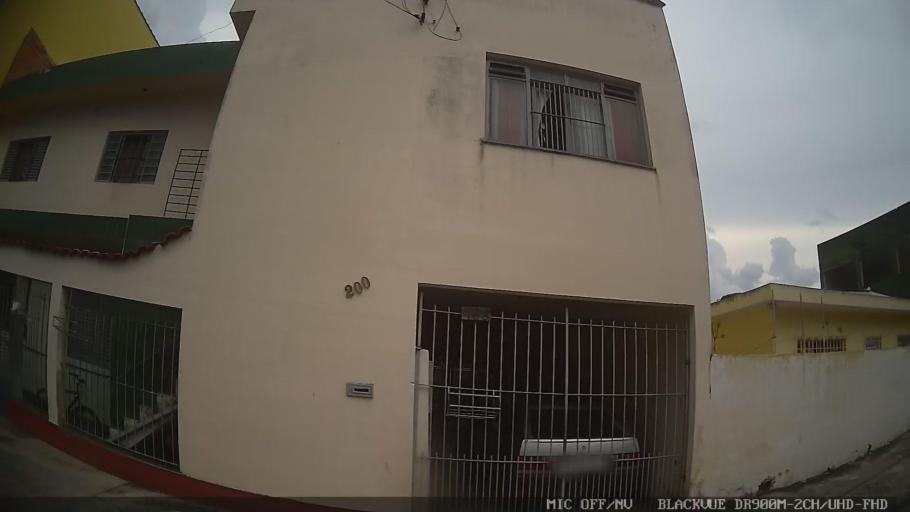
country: BR
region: Sao Paulo
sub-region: Suzano
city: Suzano
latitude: -23.5628
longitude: -46.2928
